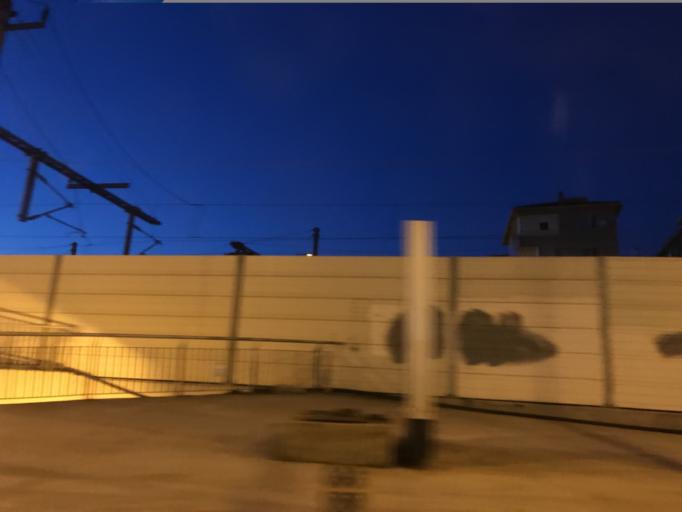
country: TR
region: Istanbul
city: Pendik
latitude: 40.8802
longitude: 29.2350
